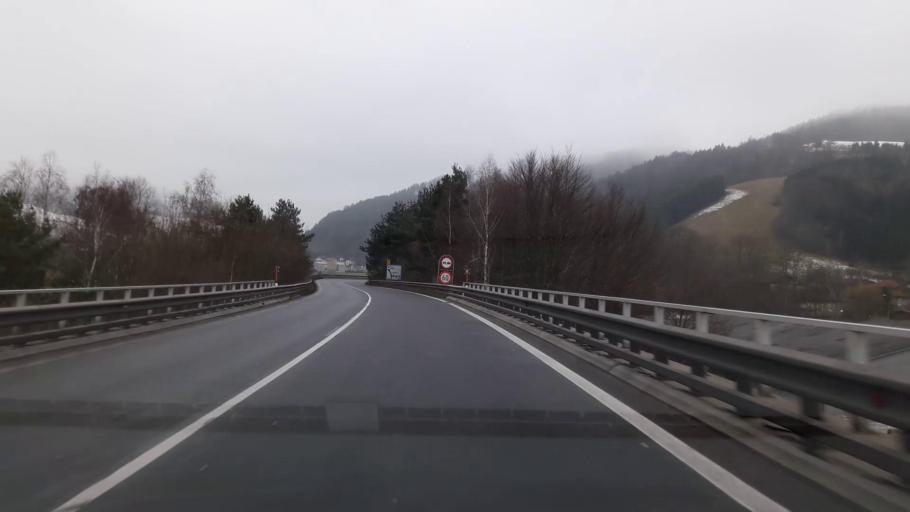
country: AT
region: Lower Austria
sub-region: Politischer Bezirk Neunkirchen
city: Grimmenstein
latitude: 47.6086
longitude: 16.1242
